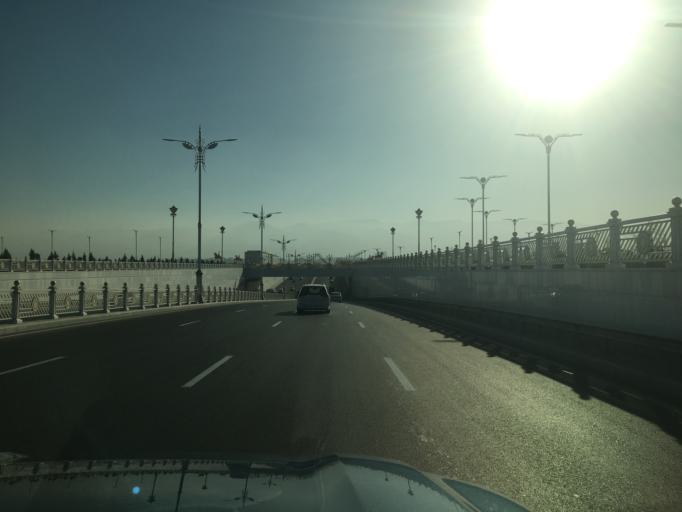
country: TM
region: Ahal
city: Ashgabat
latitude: 37.9723
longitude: 58.3893
